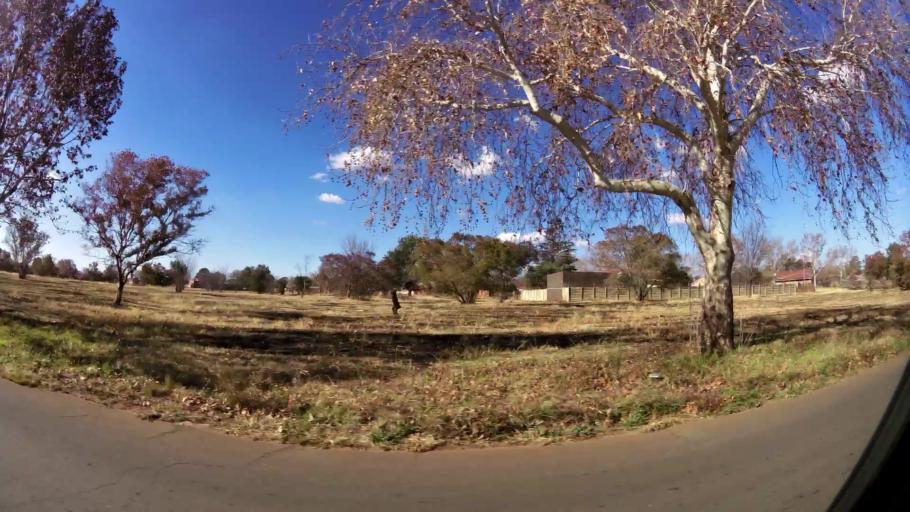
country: ZA
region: Gauteng
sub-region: West Rand District Municipality
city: Carletonville
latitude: -26.3726
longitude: 27.3969
